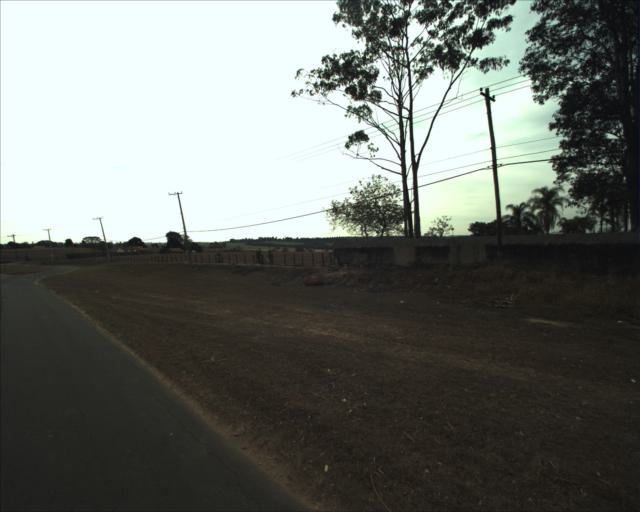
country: BR
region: Sao Paulo
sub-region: Sorocaba
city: Sorocaba
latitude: -23.4001
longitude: -47.5183
